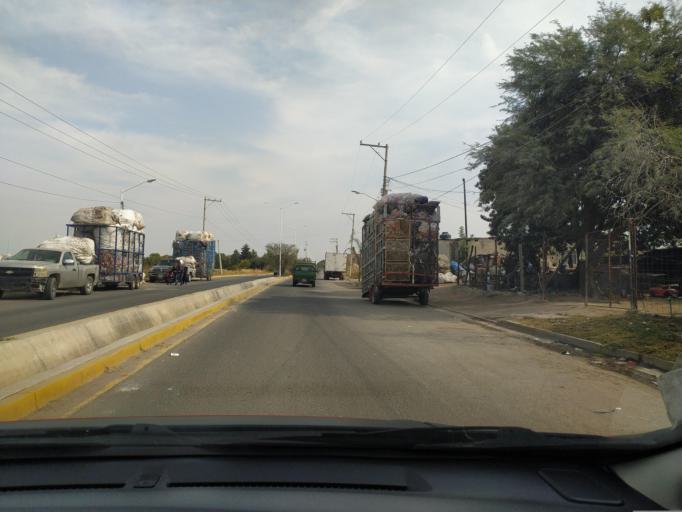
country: MX
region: Guanajuato
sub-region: San Francisco del Rincon
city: Fraccionamiento la Mezquitera
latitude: 21.0177
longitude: -101.8337
